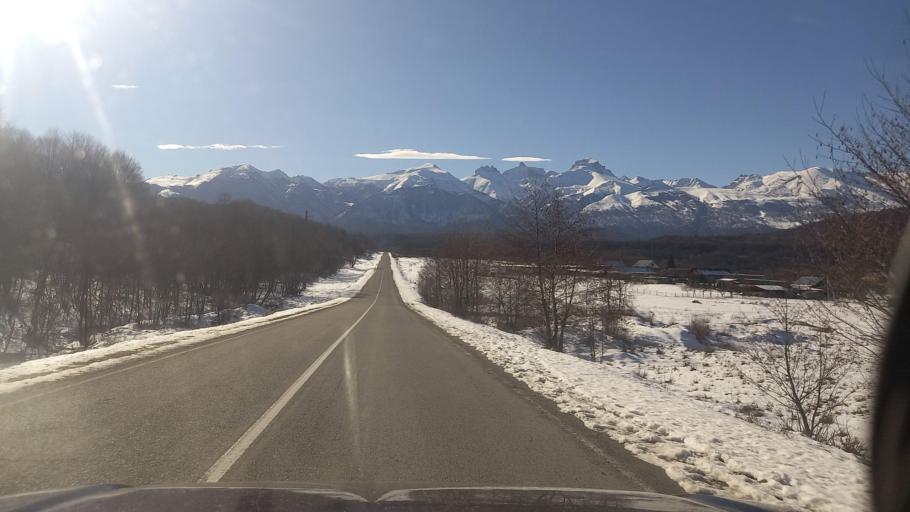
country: RU
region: North Ossetia
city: Chikola
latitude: 43.1321
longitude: 43.8227
